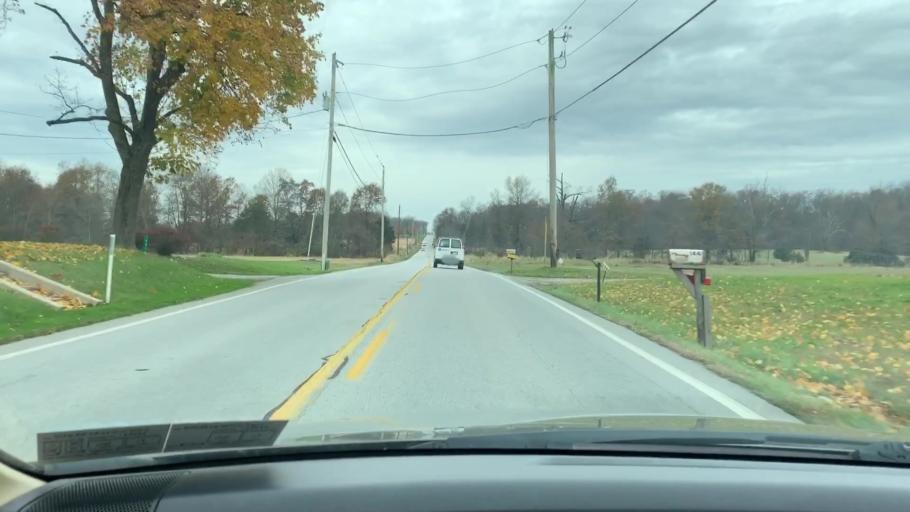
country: US
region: Pennsylvania
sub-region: Adams County
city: Lake Meade
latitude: 39.9447
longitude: -77.0849
